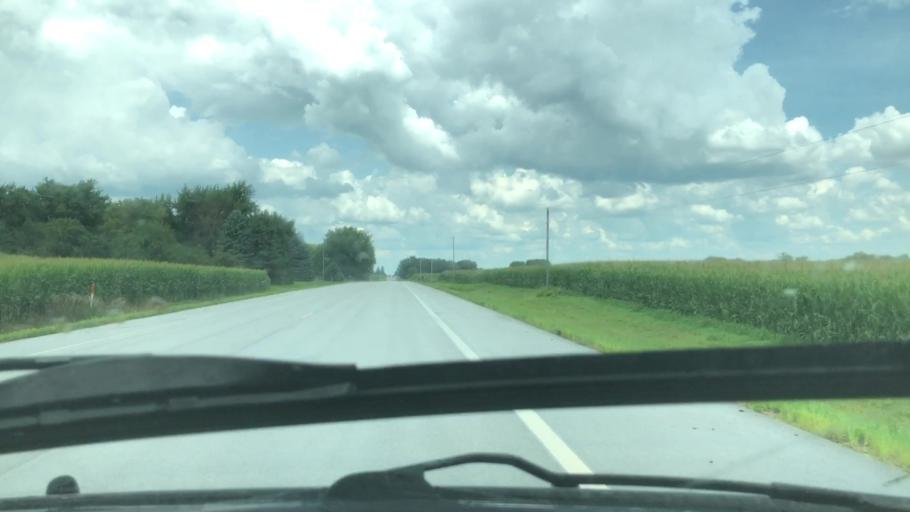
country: US
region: Minnesota
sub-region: Olmsted County
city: Stewartville
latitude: 43.9022
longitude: -92.5283
